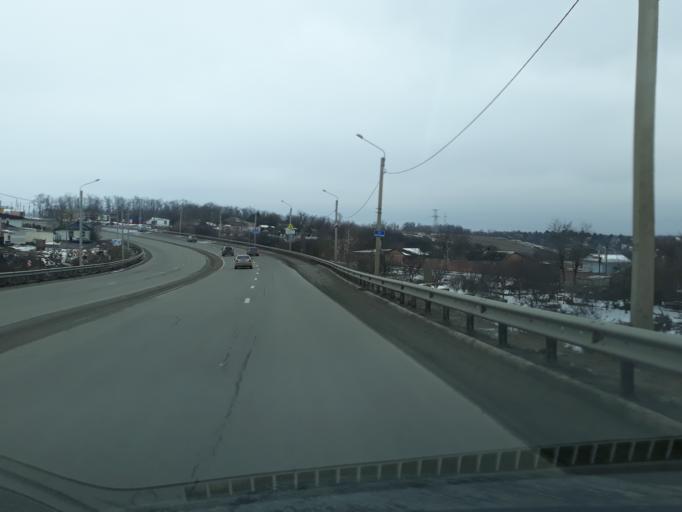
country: RU
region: Rostov
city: Sinyavskoye
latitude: 47.2996
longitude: 39.2129
